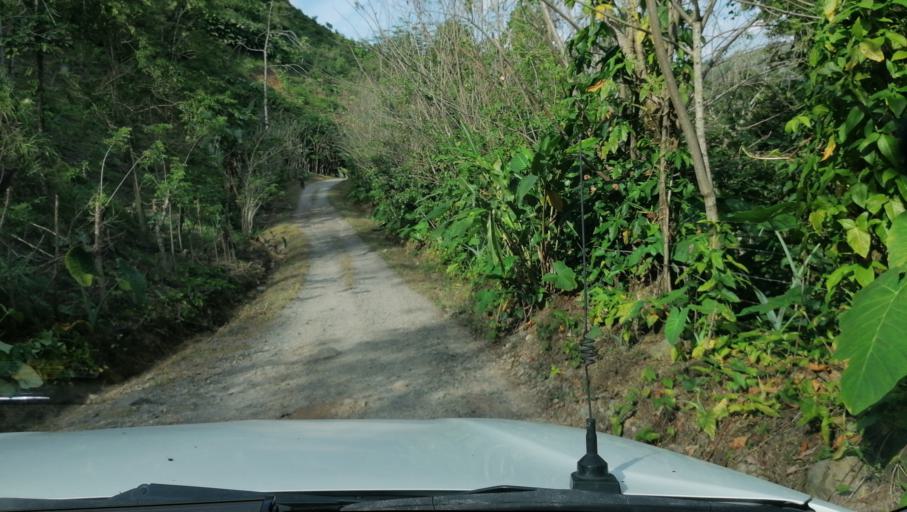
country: MX
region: Chiapas
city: Ostuacan
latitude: 17.4527
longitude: -93.2450
